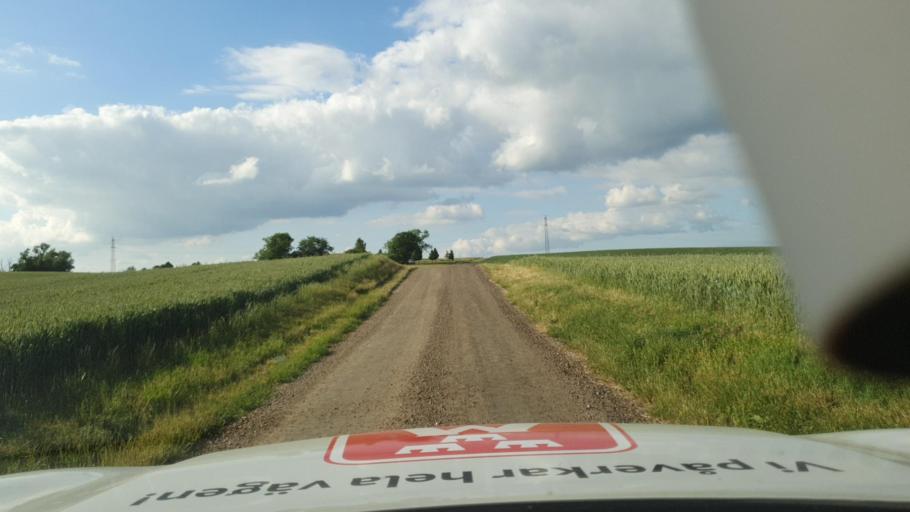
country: SE
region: Skane
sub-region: Skurups Kommun
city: Rydsgard
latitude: 55.4980
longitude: 13.5769
